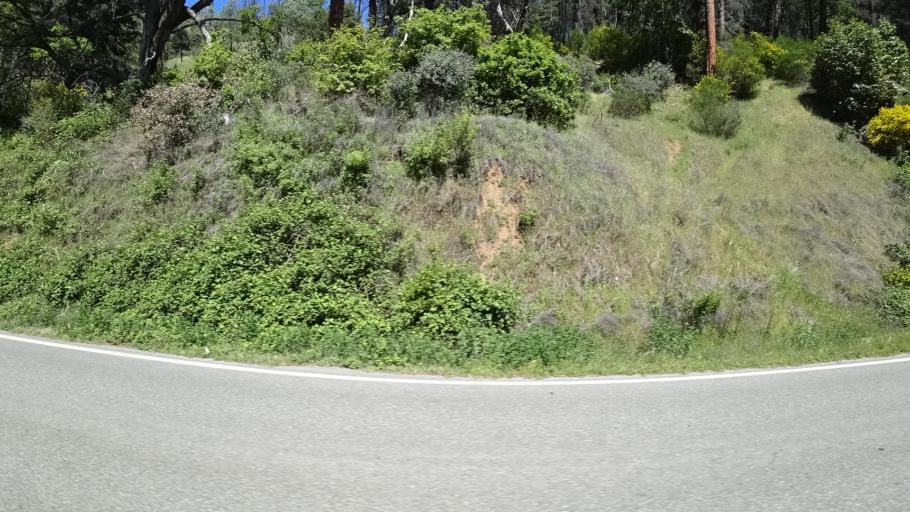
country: US
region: California
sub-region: Trinity County
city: Hayfork
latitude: 40.7484
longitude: -123.2730
